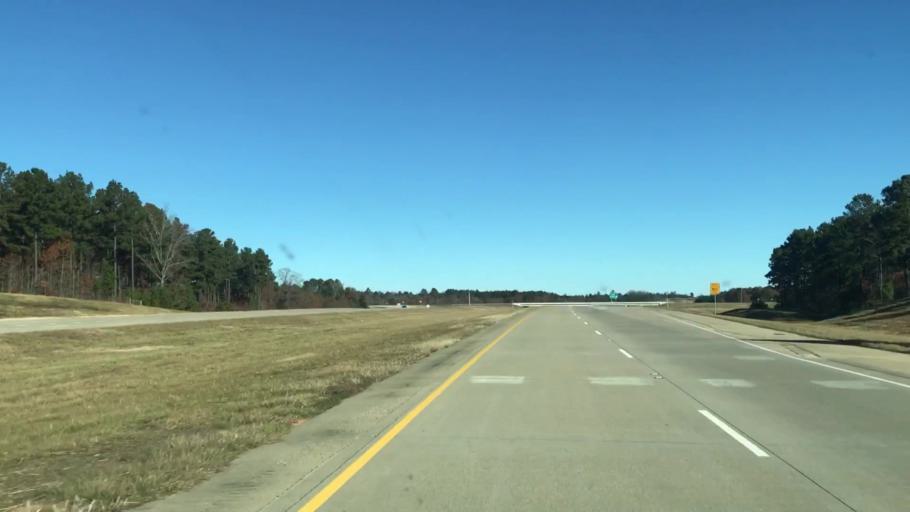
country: US
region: Louisiana
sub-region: Caddo Parish
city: Vivian
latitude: 32.9909
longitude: -93.9104
